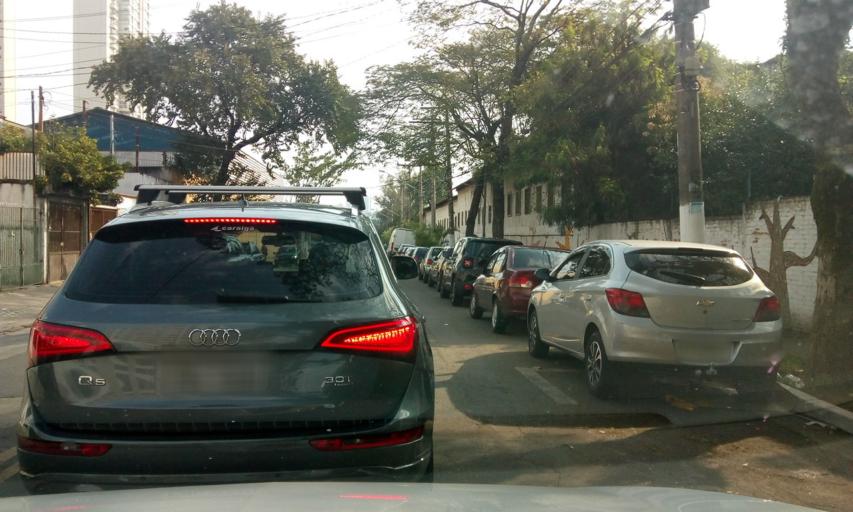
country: BR
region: Sao Paulo
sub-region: Osasco
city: Osasco
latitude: -23.5307
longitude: -46.7314
